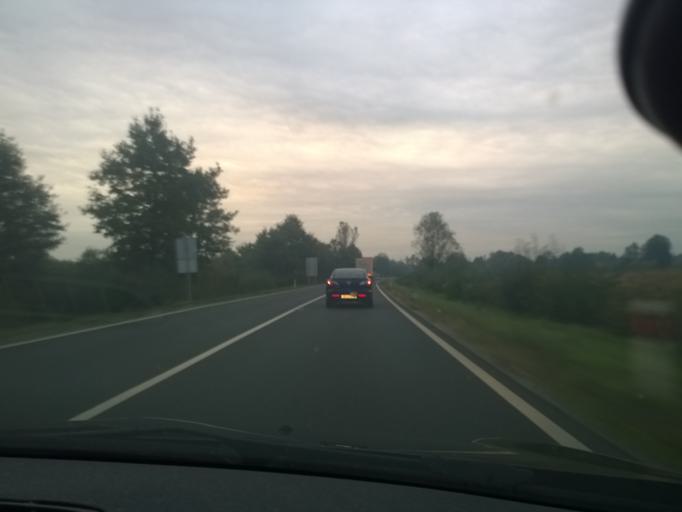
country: HR
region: Zagrebacka
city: Jakovlje
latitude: 45.9717
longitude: 15.8484
